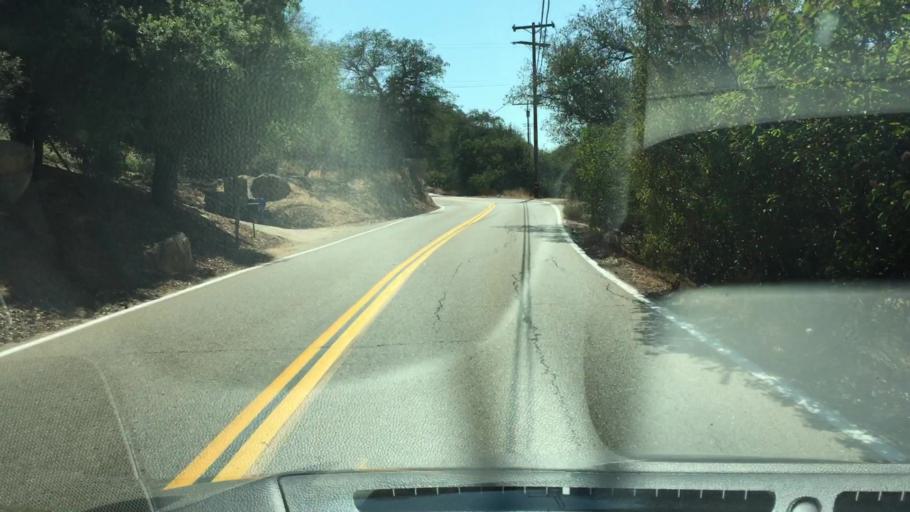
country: US
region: California
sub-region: San Diego County
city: Harbison Canyon
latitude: 32.7483
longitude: -116.7929
